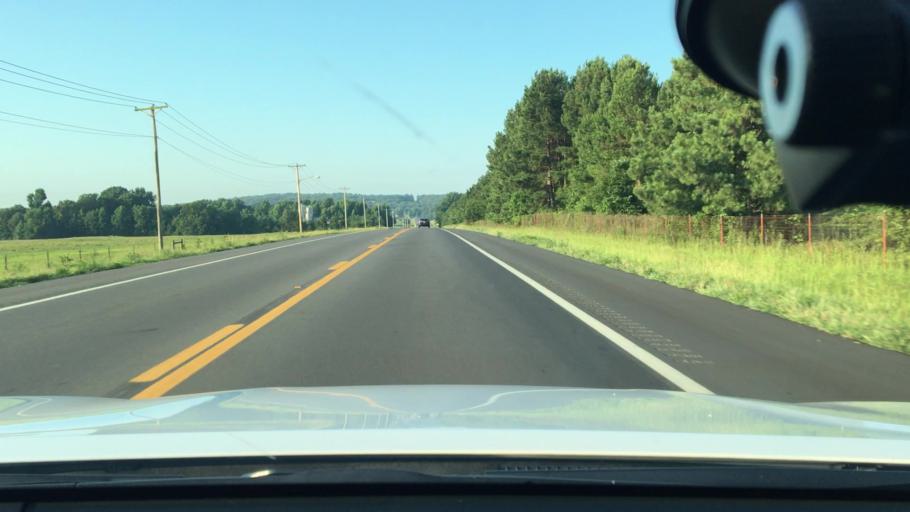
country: US
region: Arkansas
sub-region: Johnson County
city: Clarksville
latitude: 35.4409
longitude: -93.5292
